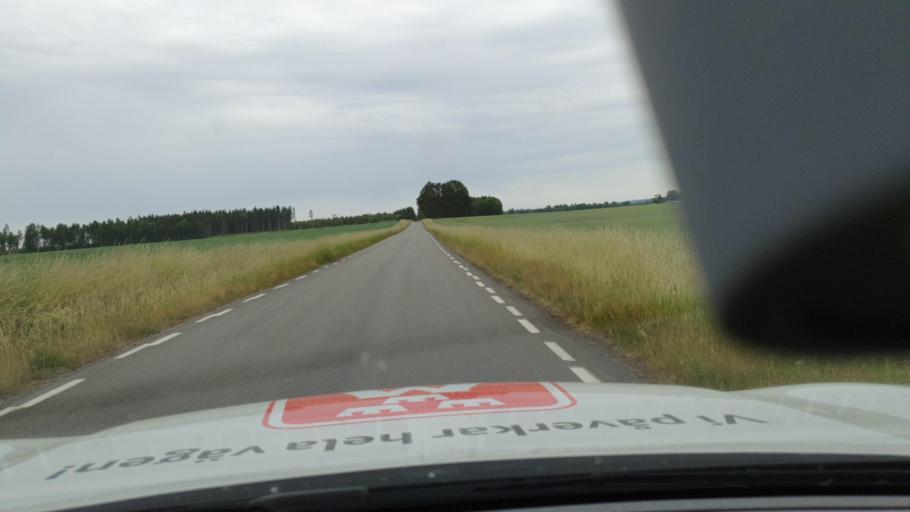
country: SE
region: Vaestra Goetaland
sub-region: Tibro Kommun
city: Tibro
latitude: 58.3323
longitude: 14.1002
